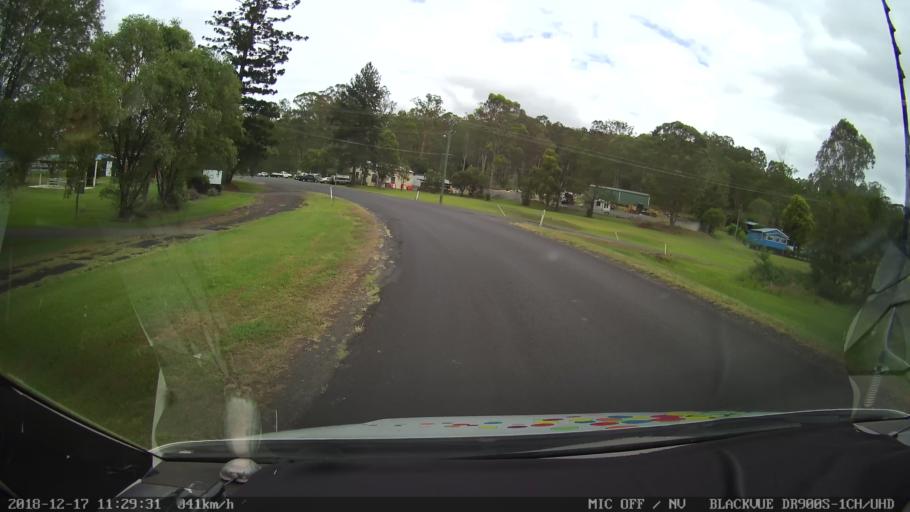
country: AU
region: New South Wales
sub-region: Kyogle
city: Kyogle
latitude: -28.7389
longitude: 152.6291
